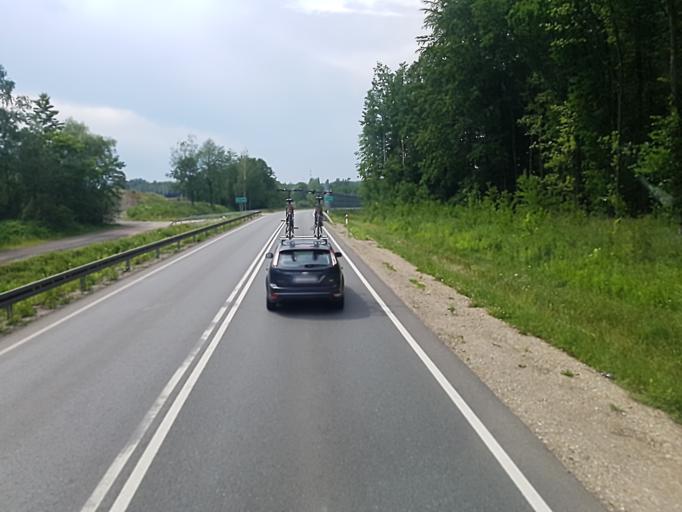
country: PL
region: Silesian Voivodeship
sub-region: Powiat pszczynski
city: Pawlowice
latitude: 49.9552
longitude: 18.6881
